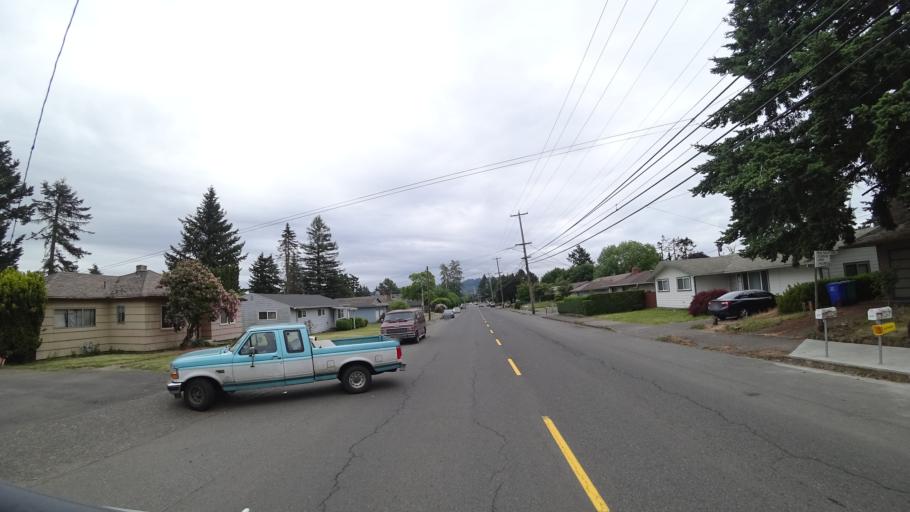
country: US
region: Oregon
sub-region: Multnomah County
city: Lents
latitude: 45.4992
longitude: -122.5480
